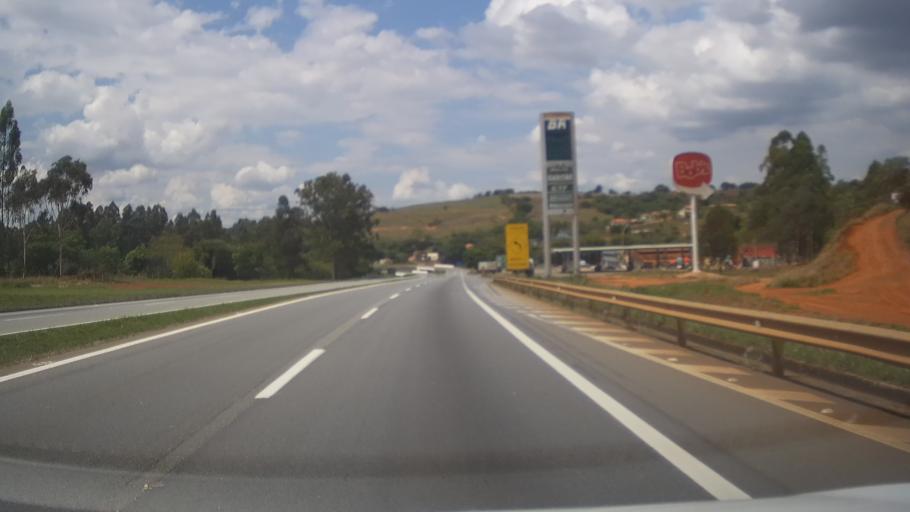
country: BR
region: Minas Gerais
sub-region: Nepomuceno
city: Nepomuceno
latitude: -21.3021
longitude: -45.1538
